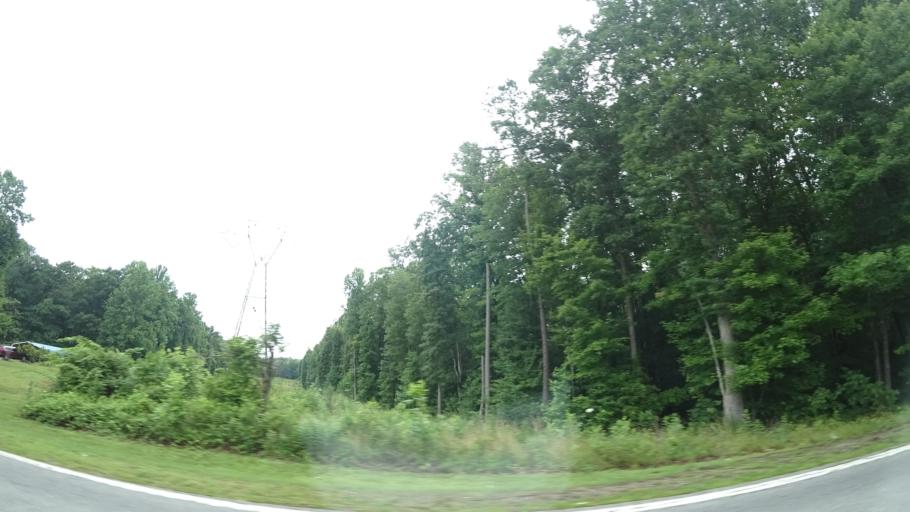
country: US
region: Virginia
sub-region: Spotsylvania County
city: Spotsylvania
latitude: 38.1345
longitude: -77.7900
